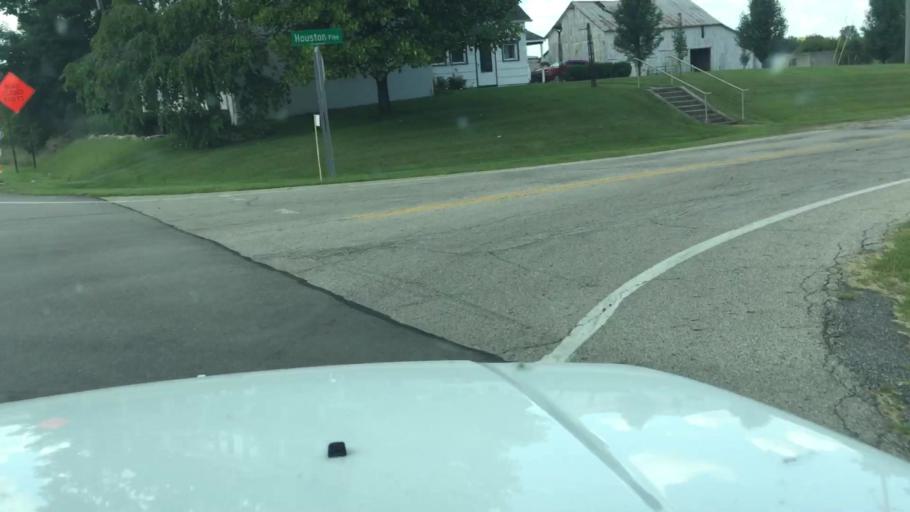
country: US
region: Ohio
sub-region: Madison County
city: Choctaw Lake
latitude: 39.9300
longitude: -83.5635
